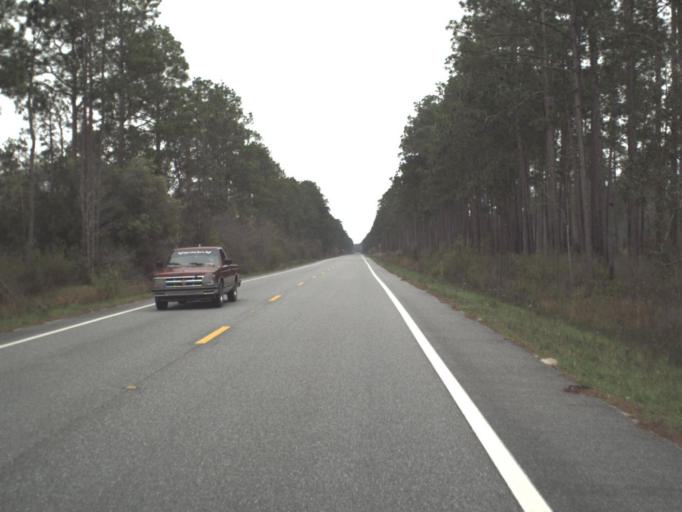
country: US
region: Florida
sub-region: Franklin County
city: Apalachicola
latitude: 29.8734
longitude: -84.9754
